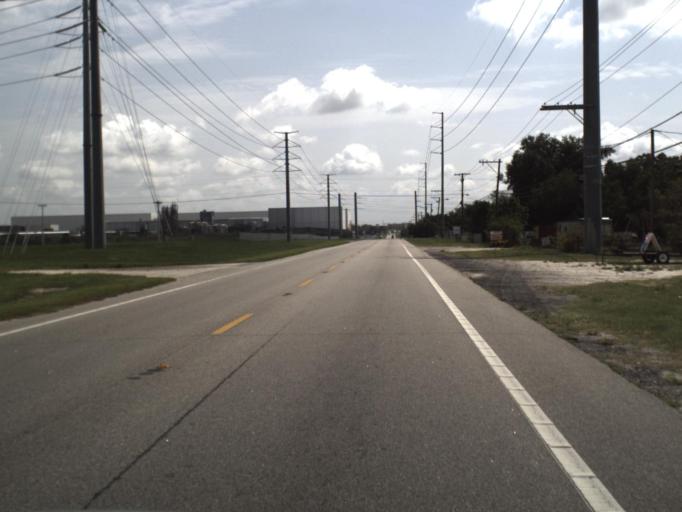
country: US
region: Florida
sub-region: Polk County
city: Auburndale
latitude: 28.0514
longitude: -81.8067
